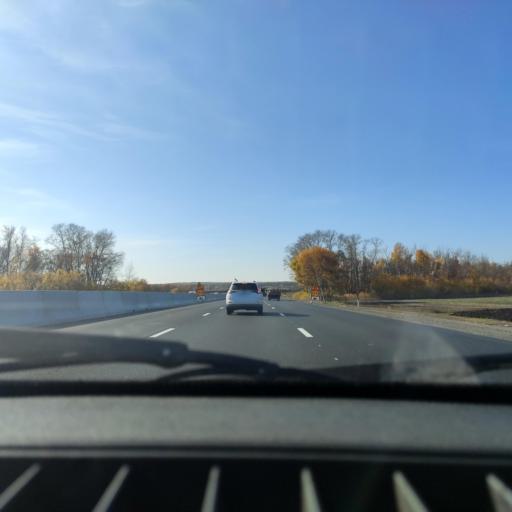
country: RU
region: Bashkortostan
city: Avdon
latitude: 54.6690
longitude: 55.7620
